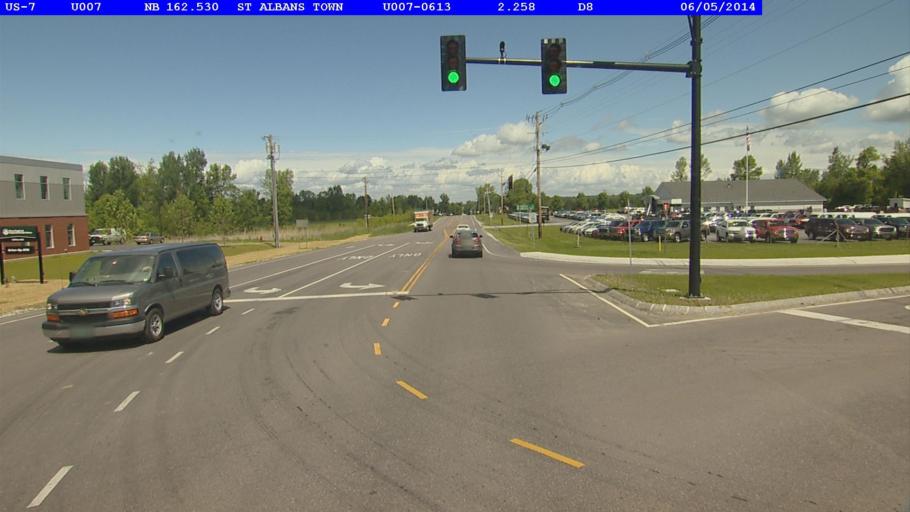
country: US
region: Vermont
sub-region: Franklin County
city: Saint Albans
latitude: 44.8407
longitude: -73.0833
